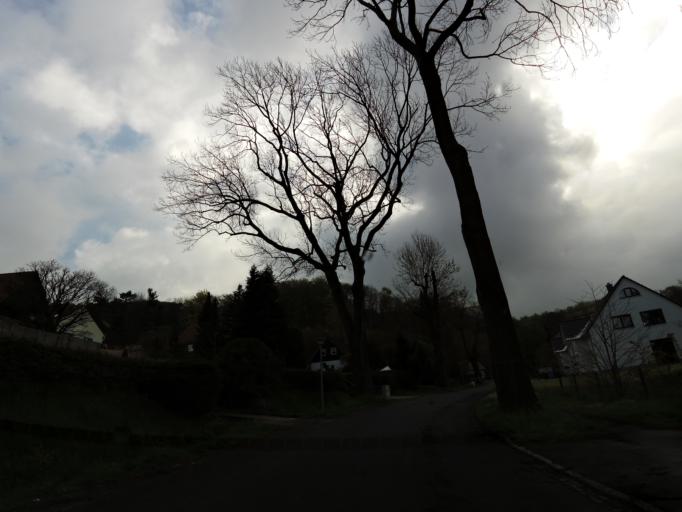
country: DE
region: Lower Saxony
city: Bovenden
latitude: 51.6004
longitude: 9.9478
